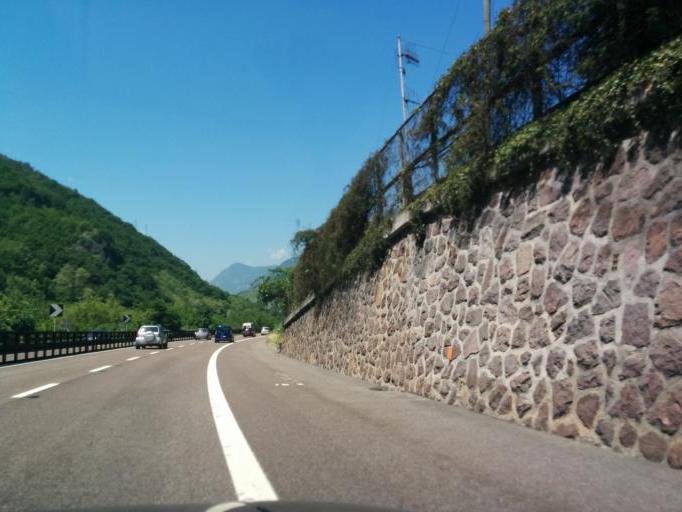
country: IT
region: Trentino-Alto Adige
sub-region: Bolzano
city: Cornedo All'Isarco
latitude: 46.4896
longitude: 11.4223
